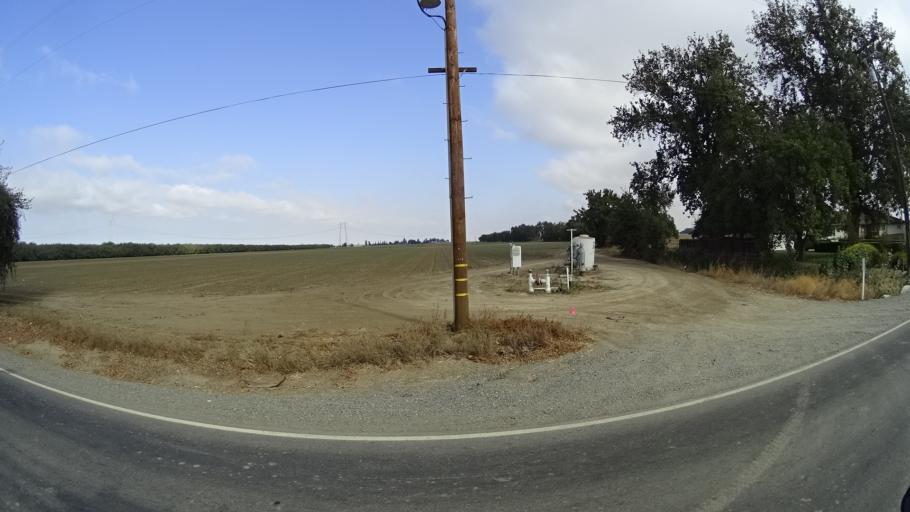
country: US
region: California
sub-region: Yolo County
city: Dunnigan
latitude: 38.7942
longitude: -121.8690
